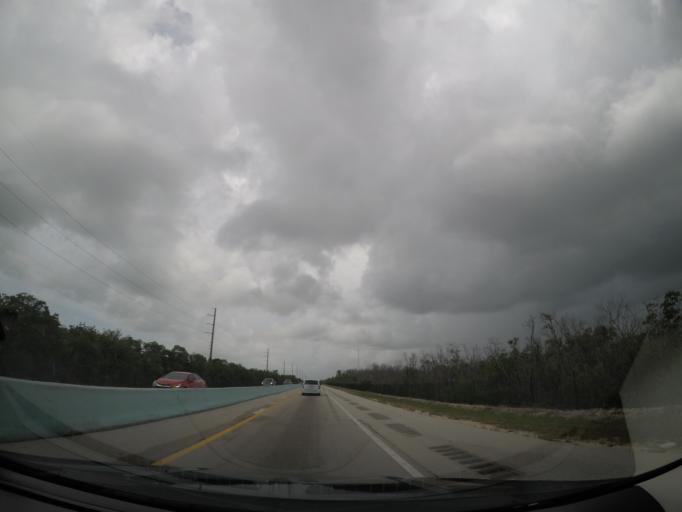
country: US
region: Florida
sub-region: Monroe County
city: North Key Largo
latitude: 25.2081
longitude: -80.4224
